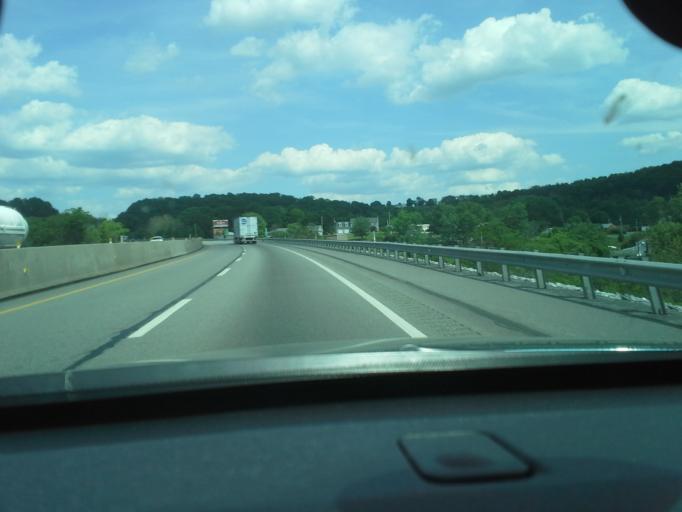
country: US
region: Pennsylvania
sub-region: Bedford County
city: Earlston
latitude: 40.0005
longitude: -78.3601
